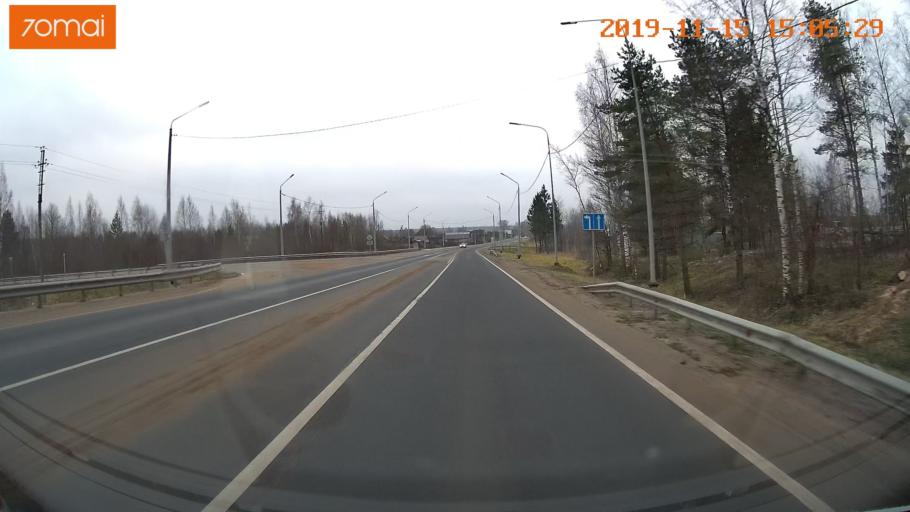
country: RU
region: Jaroslavl
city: Prechistoye
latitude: 58.4030
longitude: 40.3235
